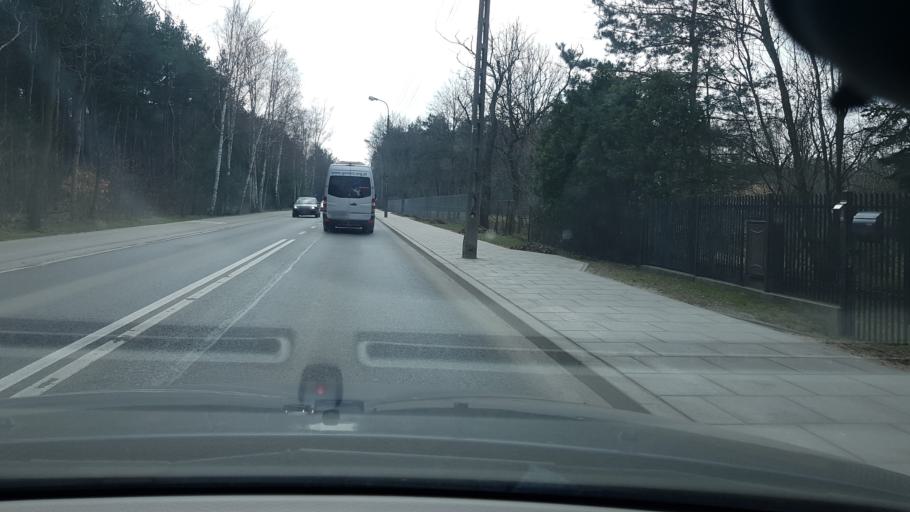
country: PL
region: Masovian Voivodeship
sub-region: Warszawa
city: Wesola
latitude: 52.2418
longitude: 21.2227
